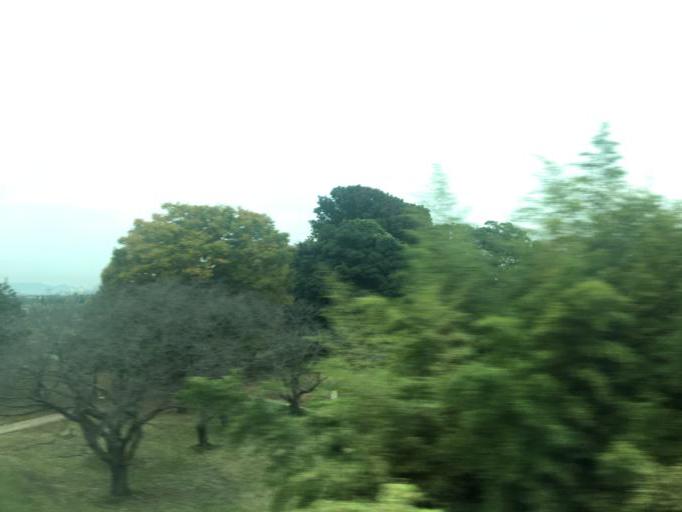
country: JP
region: Saitama
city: Kamifukuoka
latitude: 35.9099
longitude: 139.5533
